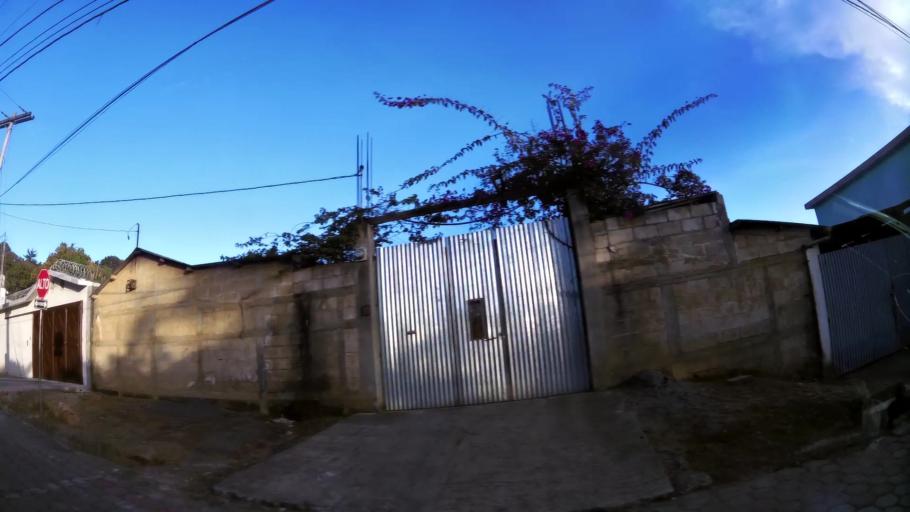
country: GT
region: Sacatepequez
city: San Lucas Sacatepequez
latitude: 14.6131
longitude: -90.6531
